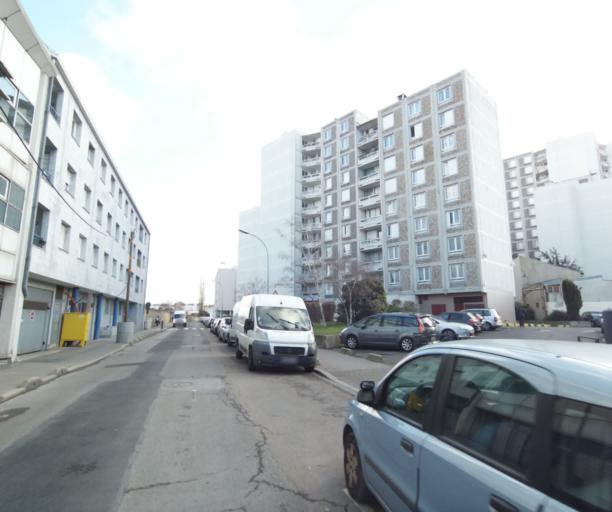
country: FR
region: Ile-de-France
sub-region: Paris
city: Saint-Ouen
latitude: 48.9123
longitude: 2.3365
